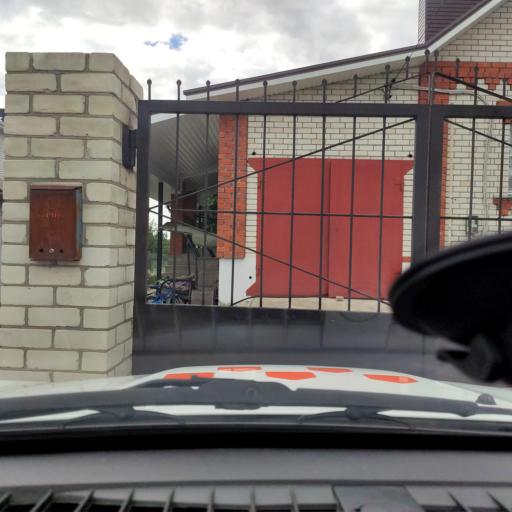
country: RU
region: Voronezj
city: Ramon'
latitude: 51.8297
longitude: 39.2596
